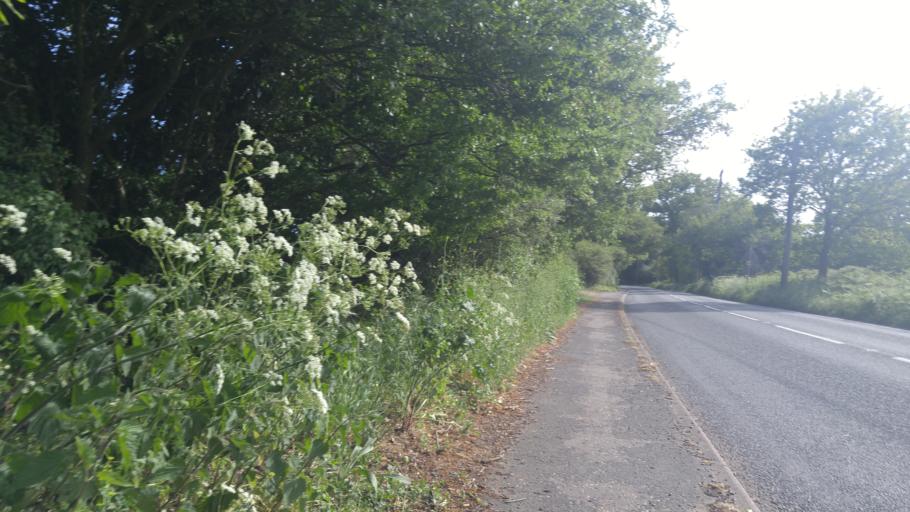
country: GB
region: England
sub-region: Essex
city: Layer de la Haye
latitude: 51.8623
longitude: 0.8680
